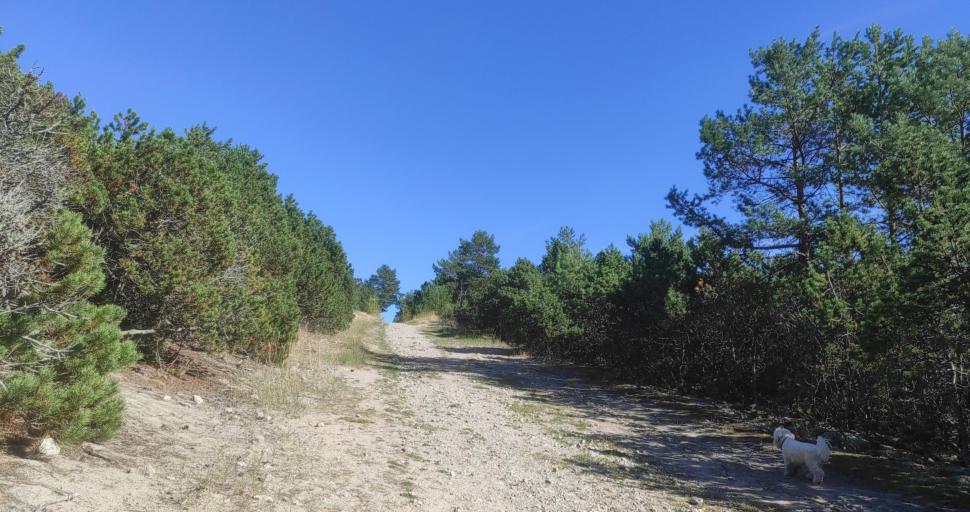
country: LT
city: Neringa
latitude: 55.3542
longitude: 21.0295
